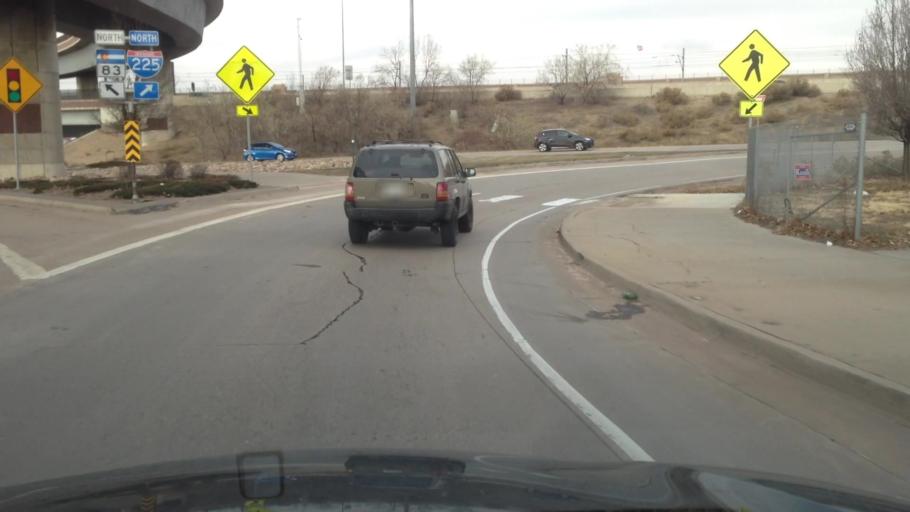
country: US
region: Colorado
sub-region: Adams County
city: Aurora
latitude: 39.6584
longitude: -104.8412
